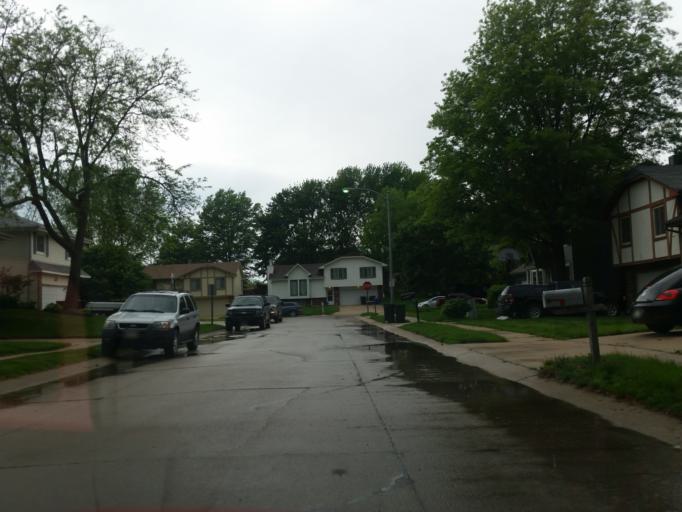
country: US
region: Nebraska
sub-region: Sarpy County
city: Offutt Air Force Base
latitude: 41.1151
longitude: -95.9700
